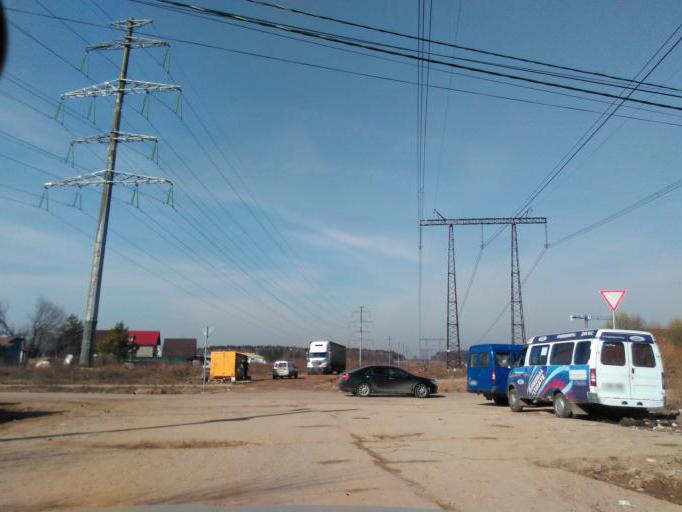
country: RU
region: Moskovskaya
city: Opalikha
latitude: 55.8834
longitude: 37.2645
